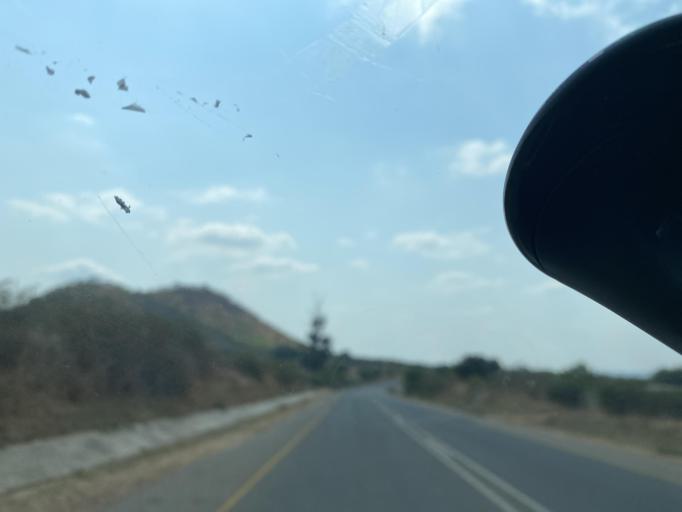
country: ZM
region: Lusaka
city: Chongwe
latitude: -15.5966
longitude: 28.7212
